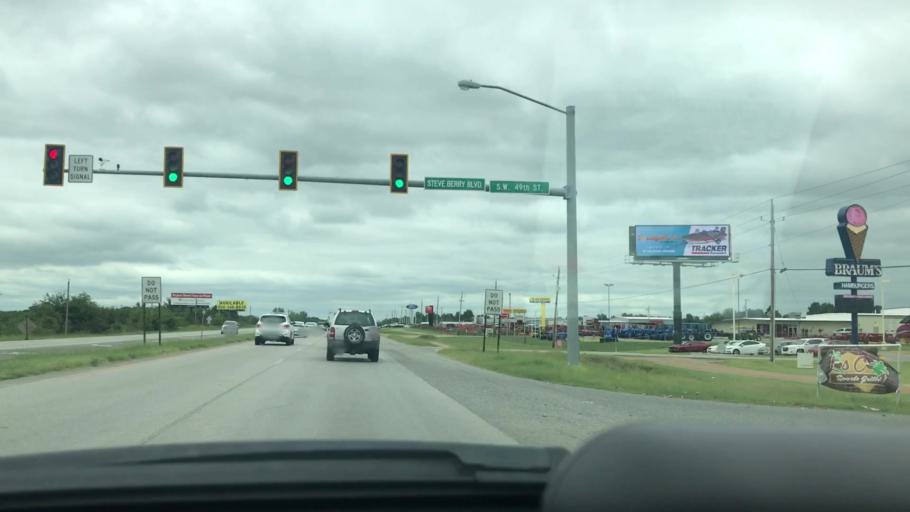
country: US
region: Oklahoma
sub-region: Mayes County
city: Pryor
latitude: 36.2639
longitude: -95.3330
